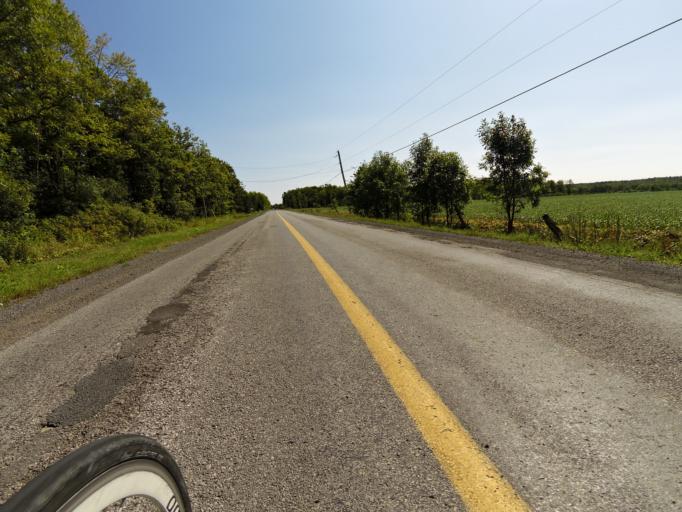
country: CA
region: Ontario
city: Bells Corners
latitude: 45.4356
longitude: -76.0643
